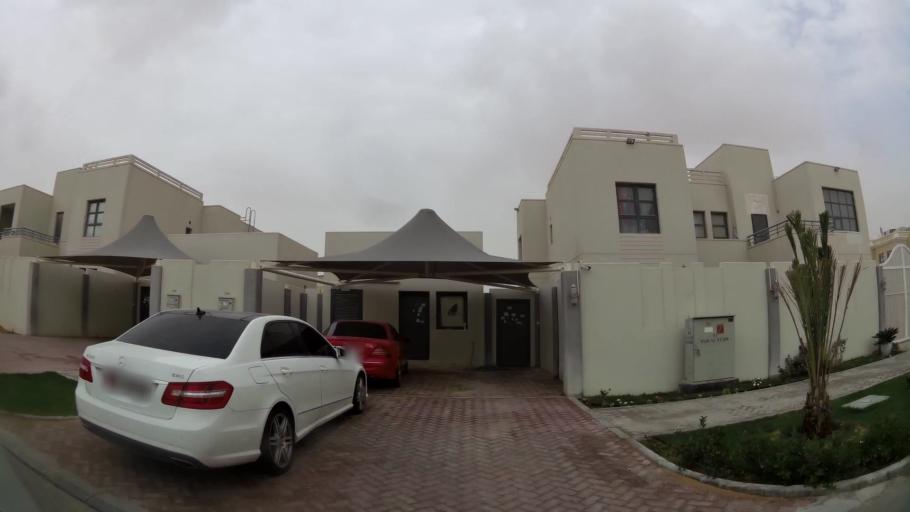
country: AE
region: Abu Dhabi
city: Abu Dhabi
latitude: 24.4543
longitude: 54.7417
